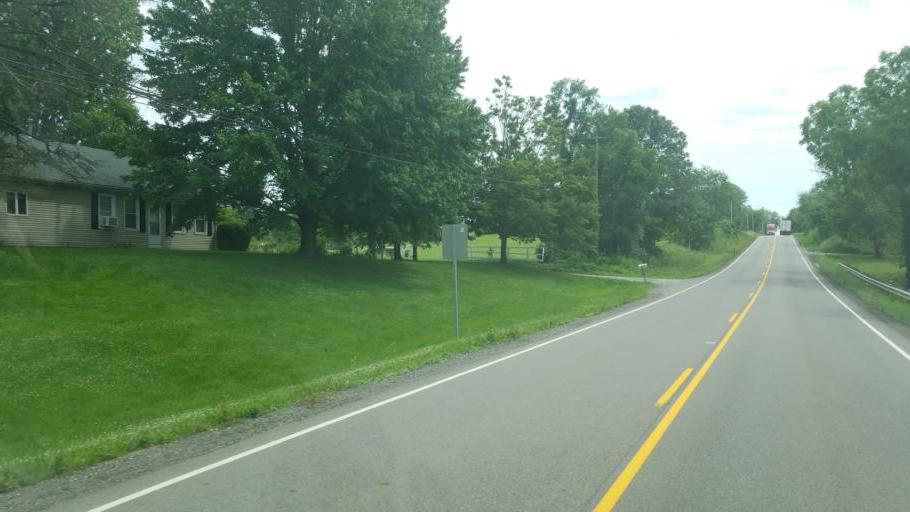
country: US
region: Ohio
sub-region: Knox County
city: Mount Vernon
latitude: 40.3090
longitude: -82.5104
